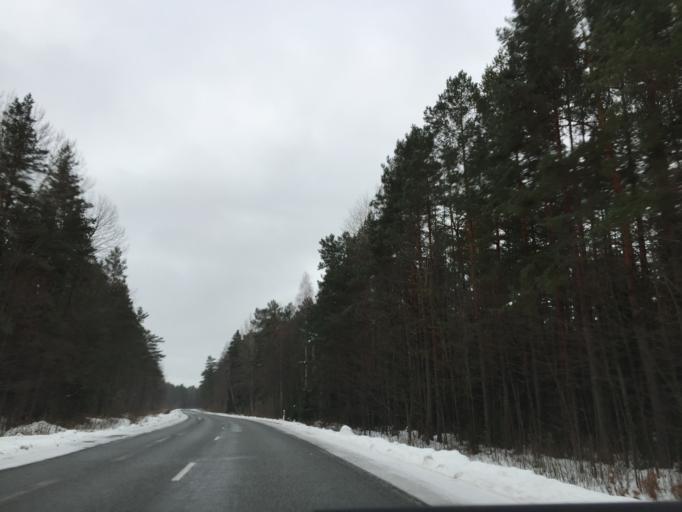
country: LV
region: Saulkrastu
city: Saulkrasti
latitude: 57.2145
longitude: 24.3831
